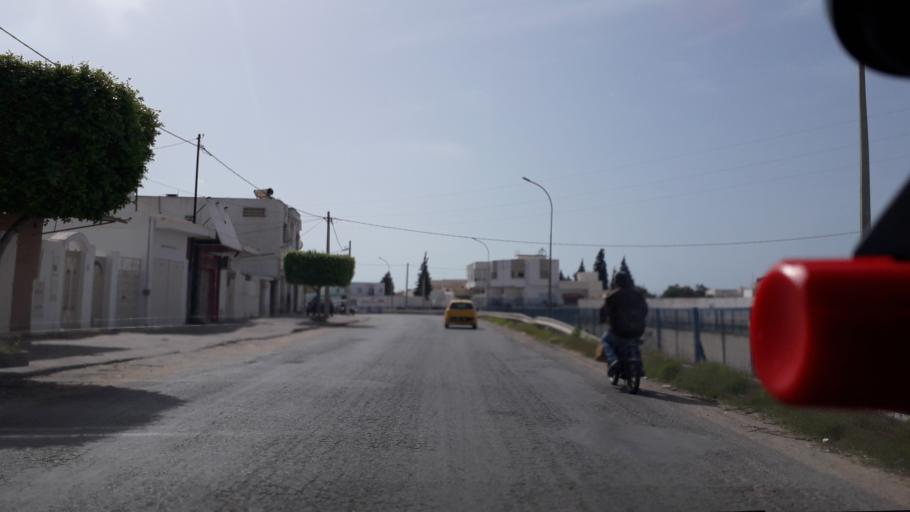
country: TN
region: Safaqis
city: Al Qarmadah
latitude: 34.8006
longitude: 10.7658
